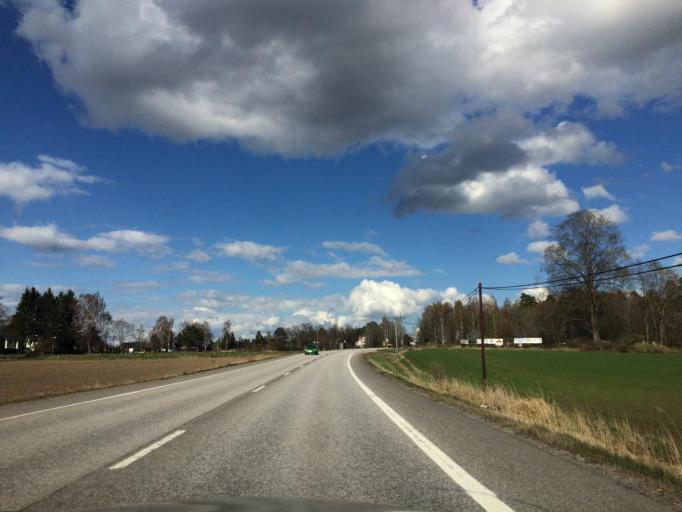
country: SE
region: Soedermanland
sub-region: Eskilstuna Kommun
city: Eskilstuna
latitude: 59.4287
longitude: 16.6116
